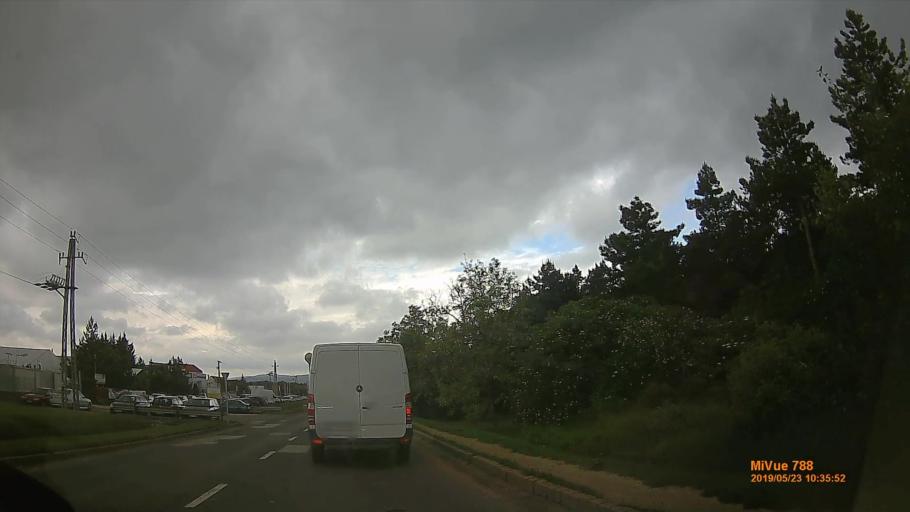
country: HU
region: Veszprem
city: Veszprem
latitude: 47.1113
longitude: 17.8871
